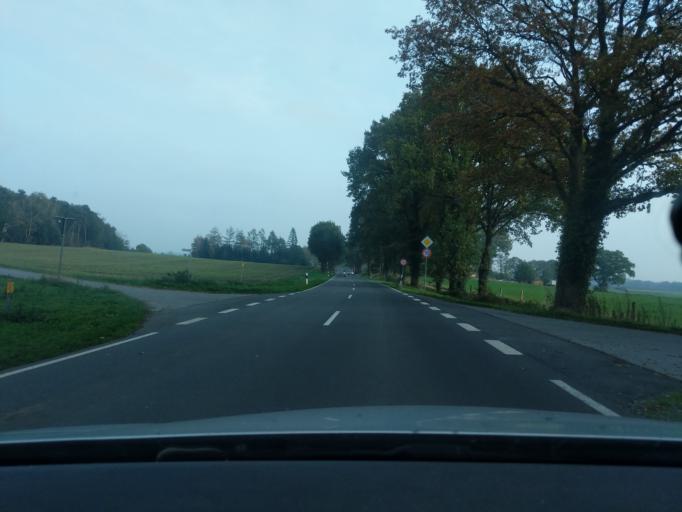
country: DE
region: Lower Saxony
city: Lamstedt
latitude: 53.6344
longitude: 9.1206
